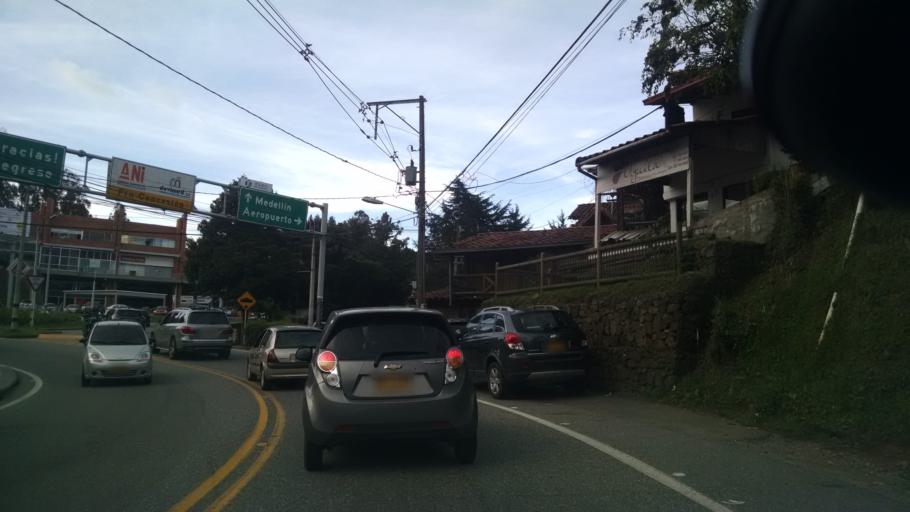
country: CO
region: Antioquia
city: Envigado
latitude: 6.1528
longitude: -75.5326
